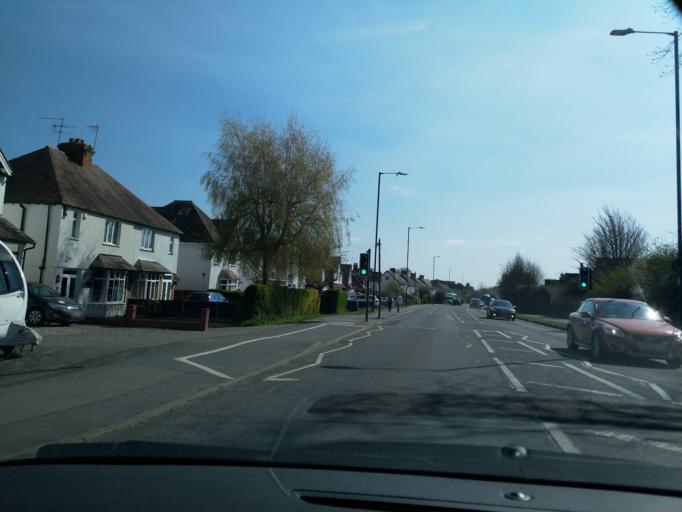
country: GB
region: England
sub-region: Warwickshire
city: Stratford-upon-Avon
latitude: 52.1953
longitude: -1.7268
